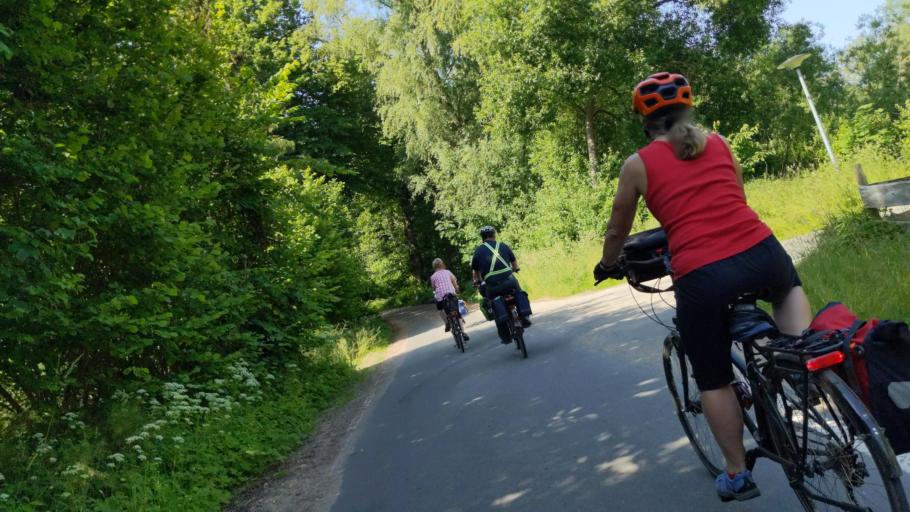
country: DE
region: Schleswig-Holstein
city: Krummesse
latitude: 53.7814
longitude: 10.6324
